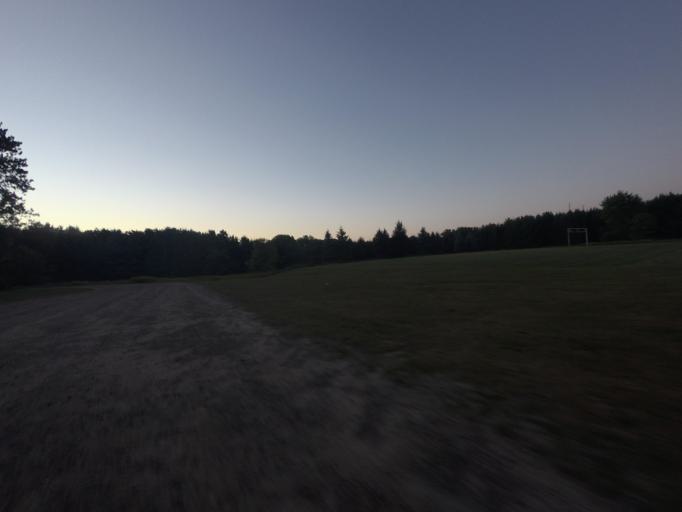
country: CA
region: Ontario
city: Bradford West Gwillimbury
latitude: 43.9633
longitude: -79.8274
